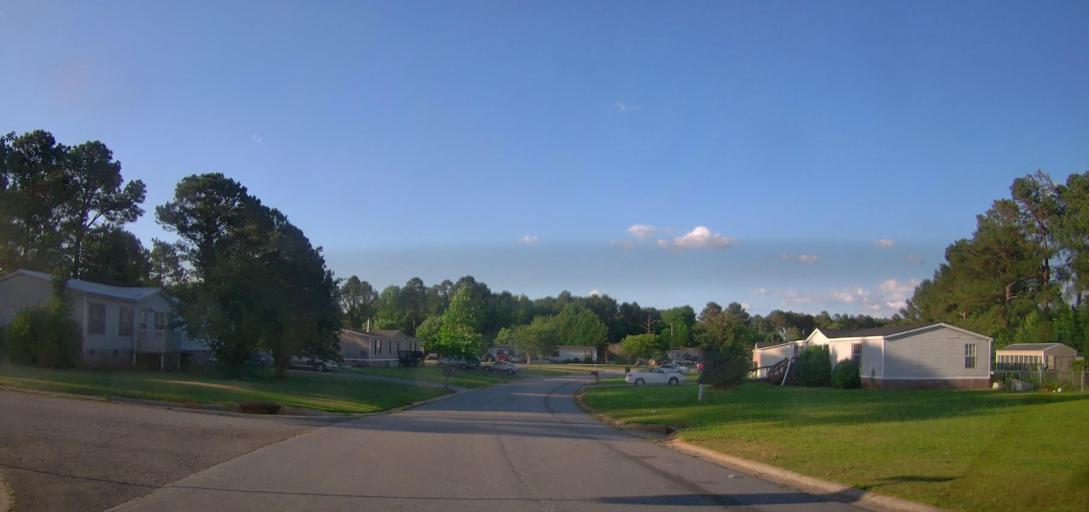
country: US
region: Georgia
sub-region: Houston County
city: Centerville
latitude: 32.6416
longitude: -83.7241
